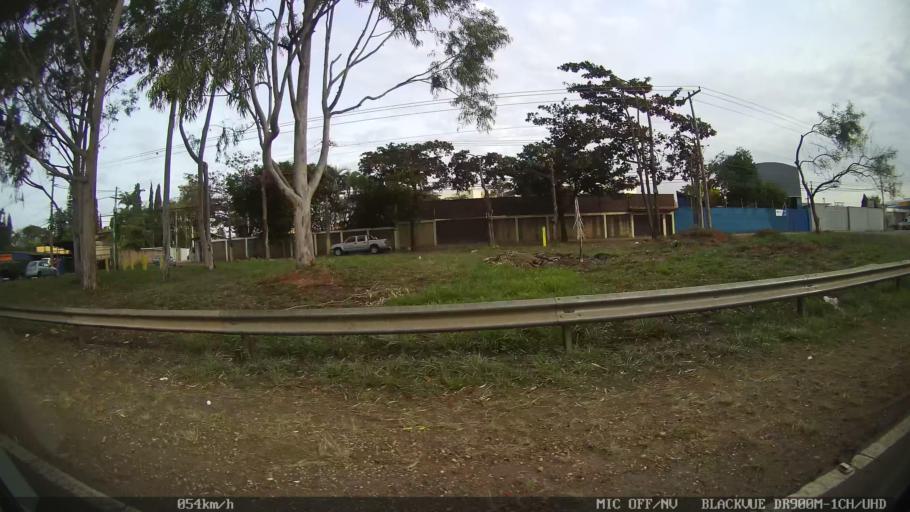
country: BR
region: Sao Paulo
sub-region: Piracicaba
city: Piracicaba
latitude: -22.7375
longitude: -47.5960
